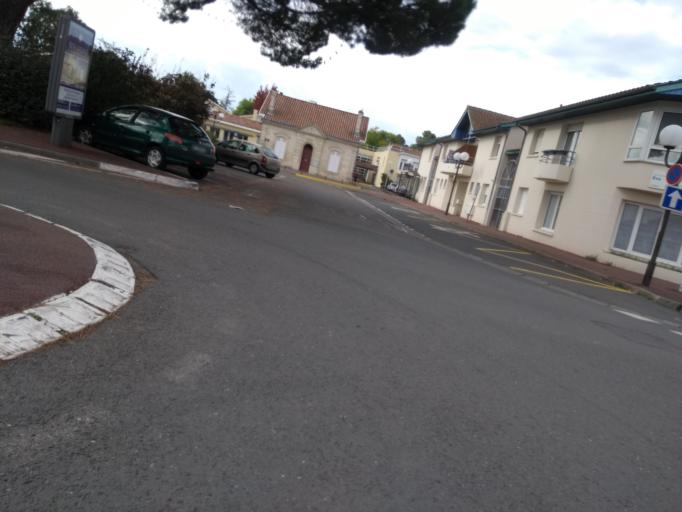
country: FR
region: Aquitaine
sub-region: Departement de la Gironde
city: Saint-Aubin-de-Medoc
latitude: 44.7722
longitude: -0.7017
